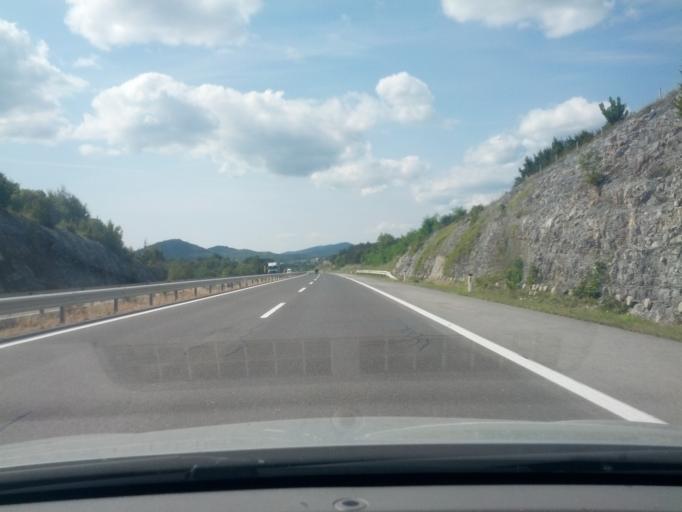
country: SI
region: Sezana
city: Sezana
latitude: 45.7117
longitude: 13.9140
